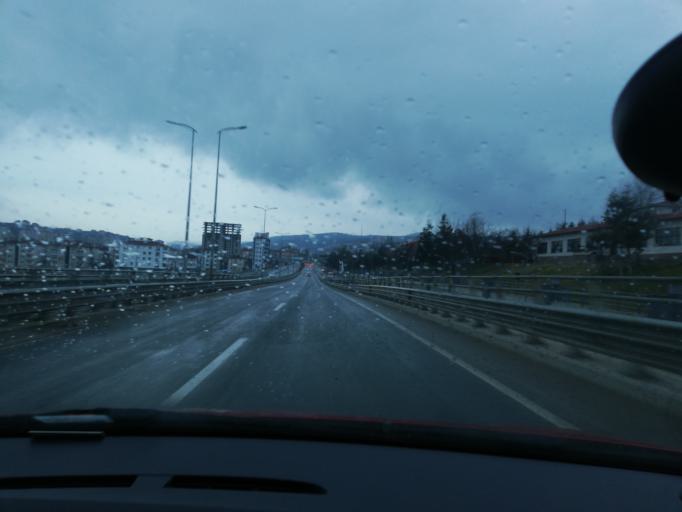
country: TR
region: Kastamonu
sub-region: Cide
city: Kastamonu
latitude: 41.4151
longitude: 33.7959
